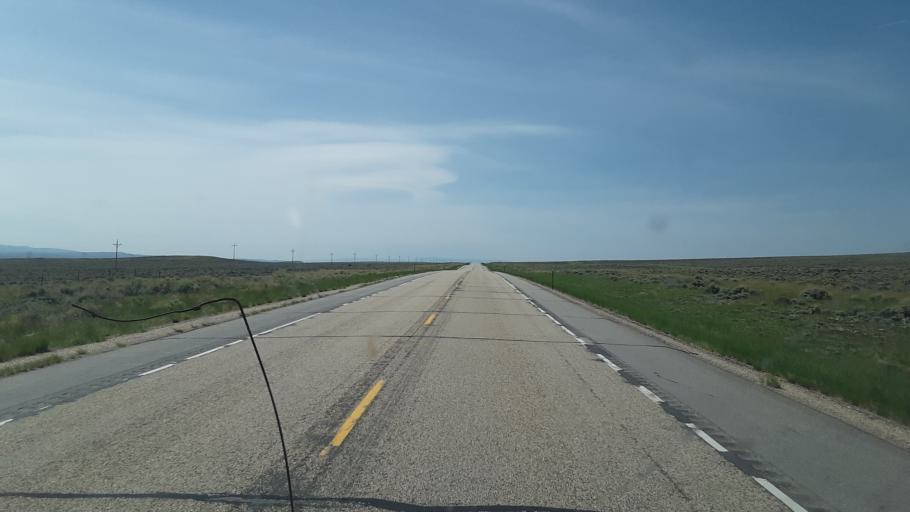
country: US
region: Wyoming
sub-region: Carbon County
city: Saratoga
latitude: 41.5826
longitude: -106.8146
